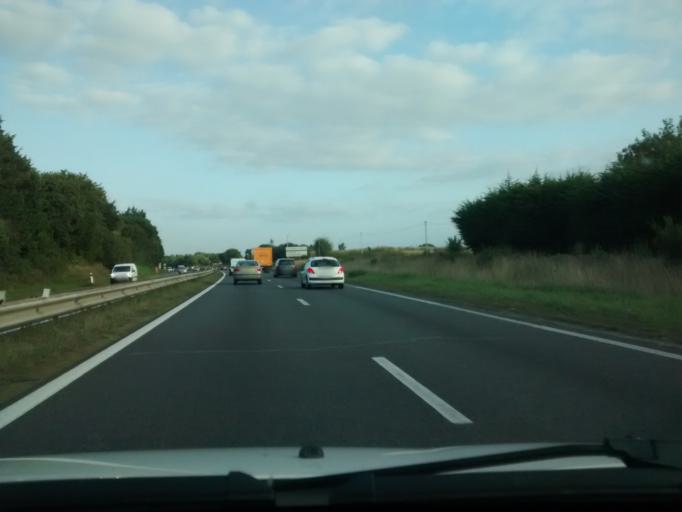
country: FR
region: Brittany
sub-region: Departement des Cotes-d'Armor
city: Plerin
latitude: 48.5387
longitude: -2.7620
